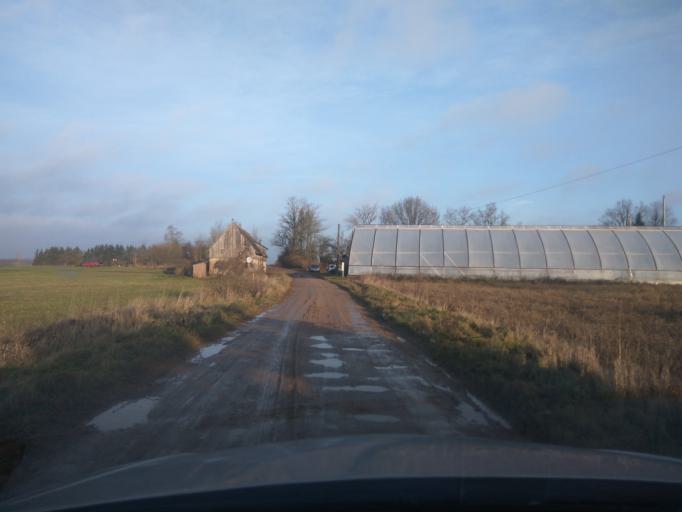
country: LV
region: Skrunda
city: Skrunda
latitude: 56.8440
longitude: 22.2213
